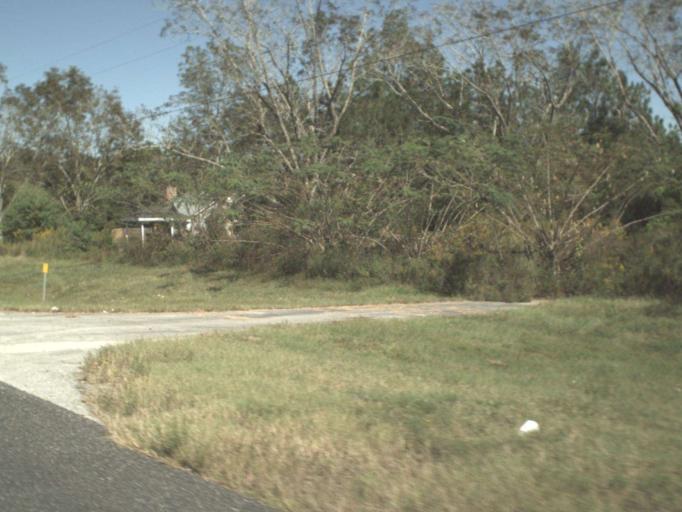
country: US
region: Florida
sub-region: Okaloosa County
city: Crestview
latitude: 30.8161
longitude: -86.5391
